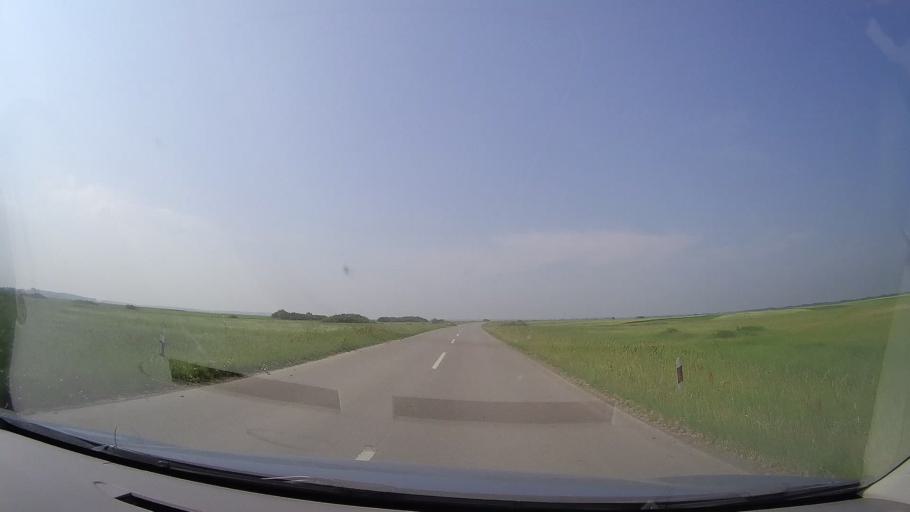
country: RS
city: Jasa Tomic
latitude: 45.4223
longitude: 20.8359
